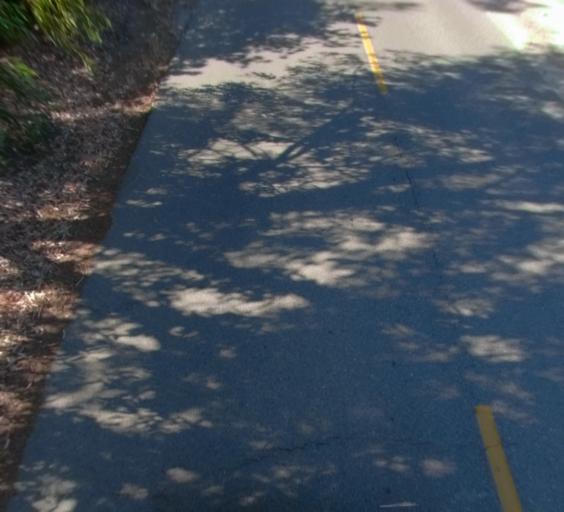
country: US
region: California
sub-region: Madera County
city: Bonadelle Ranchos-Madera Ranchos
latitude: 36.9728
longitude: -119.8902
